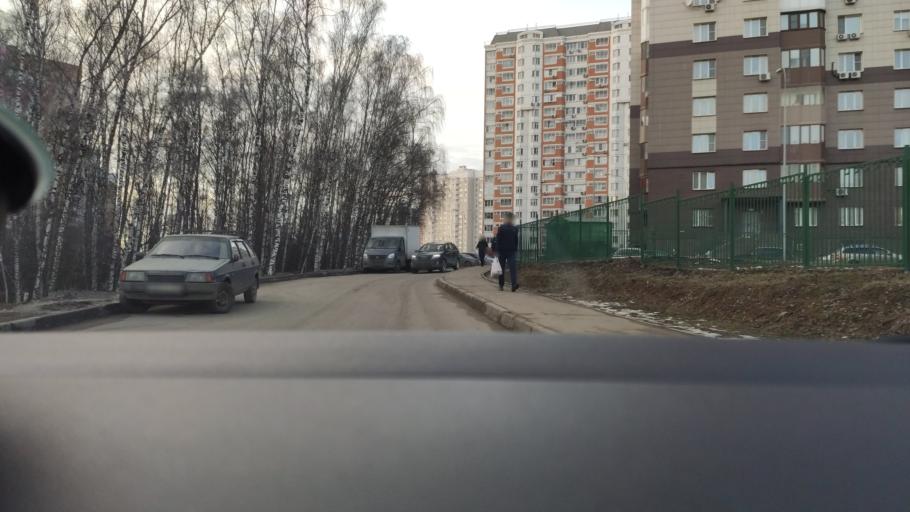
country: RU
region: Moskovskaya
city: Vidnoye
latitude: 55.5350
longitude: 37.7227
